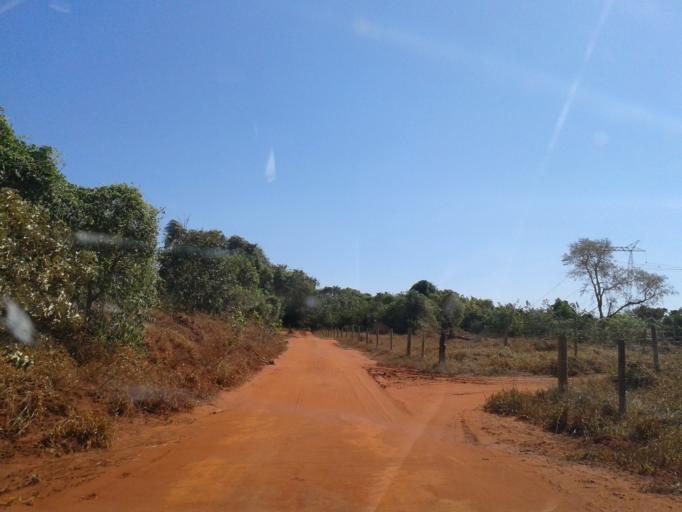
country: BR
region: Minas Gerais
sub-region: Monte Alegre De Minas
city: Monte Alegre de Minas
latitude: -18.8701
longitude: -49.1316
